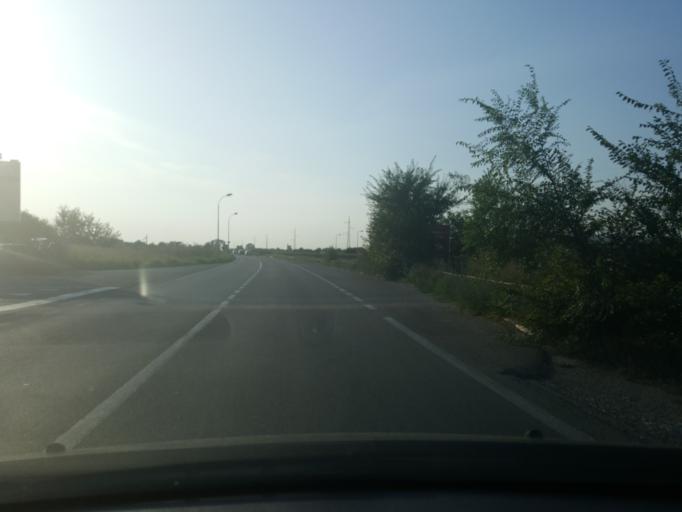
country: RS
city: Majur
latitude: 44.7628
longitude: 19.6402
